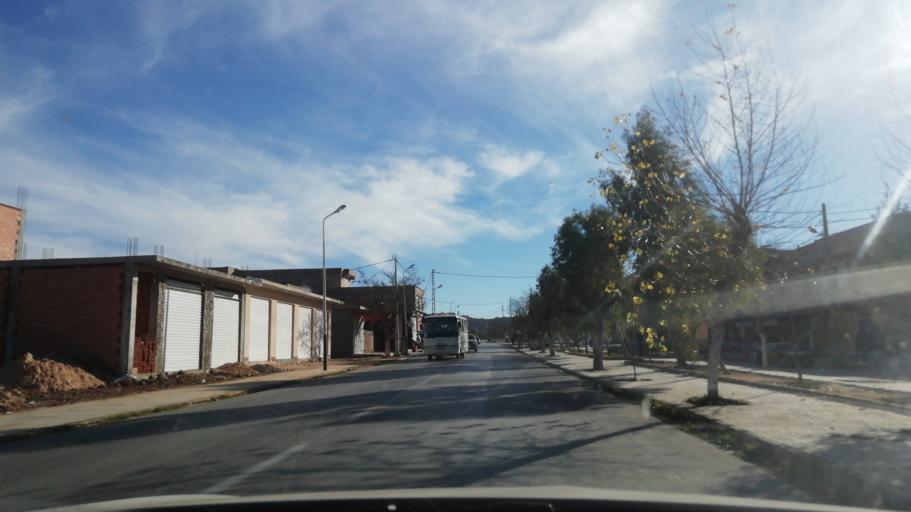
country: DZ
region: Tlemcen
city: Sebdou
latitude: 34.6284
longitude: -1.3338
